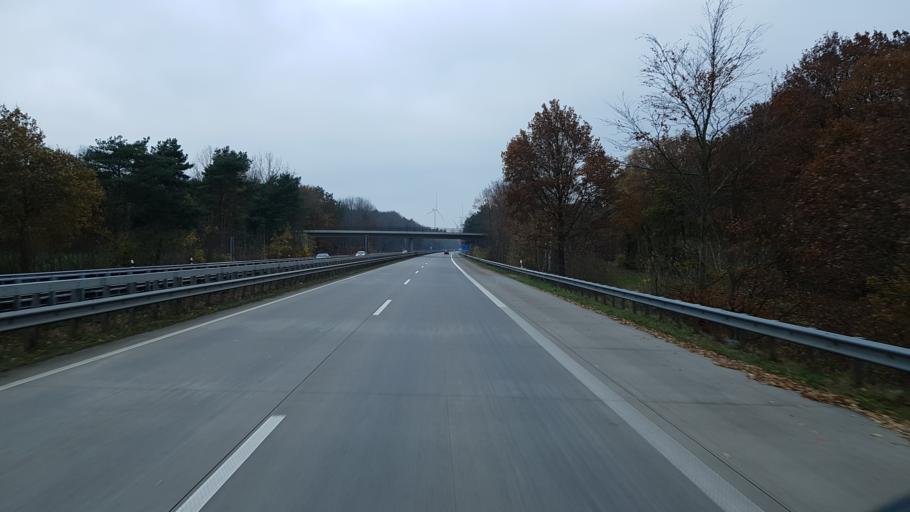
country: DE
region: Lower Saxony
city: Schwanewede
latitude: 53.2337
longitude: 8.6399
